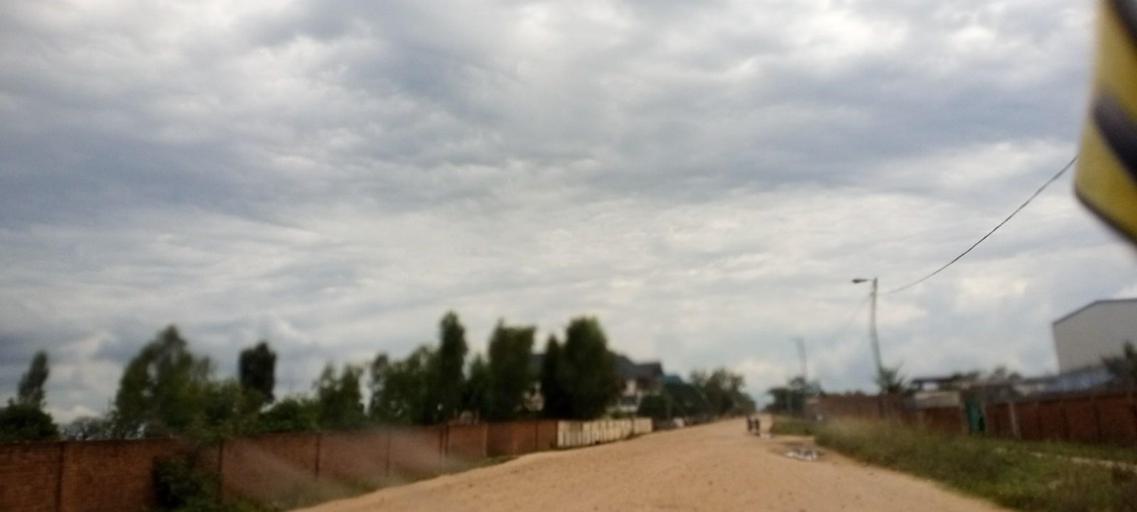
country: CD
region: South Kivu
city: Uvira
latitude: -3.3464
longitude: 29.1756
